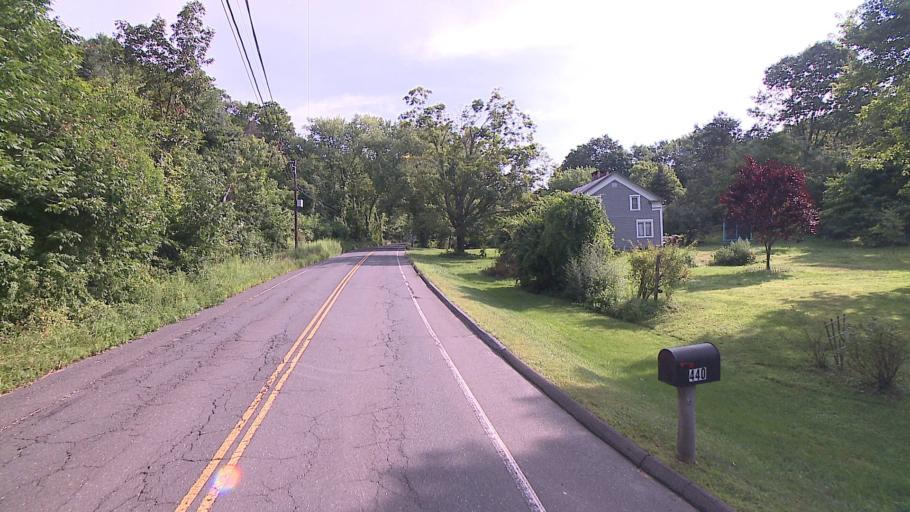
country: US
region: New York
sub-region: Putnam County
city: Putnam Lake
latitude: 41.5171
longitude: -73.5215
